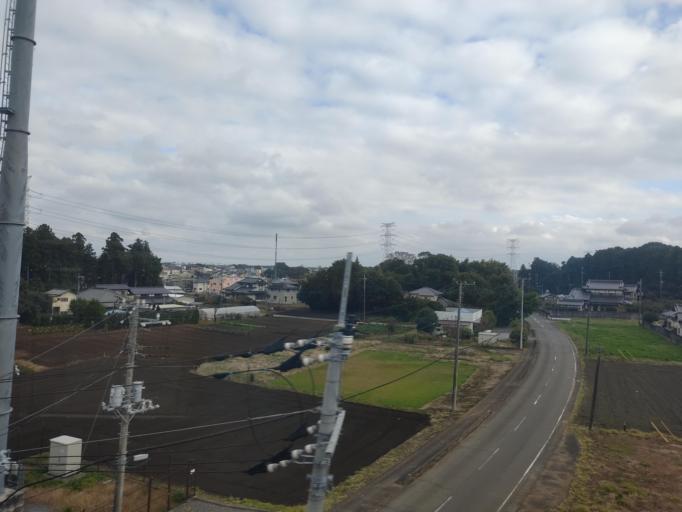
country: JP
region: Ibaraki
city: Mitsukaido
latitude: 36.0338
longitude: 140.0572
